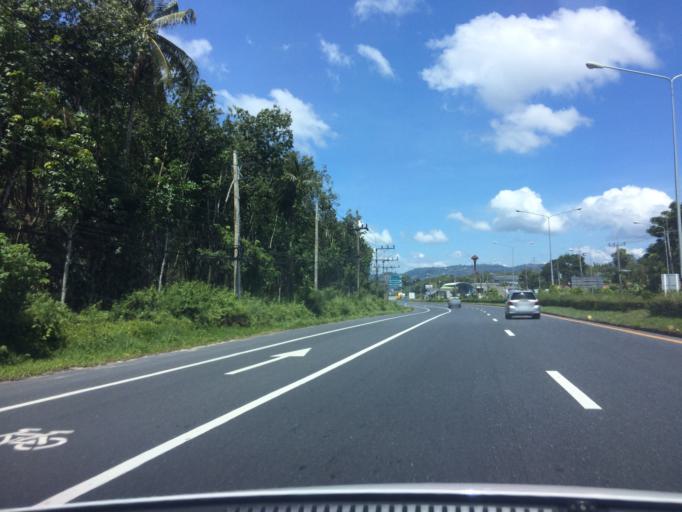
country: TH
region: Phangnga
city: Thai Mueang
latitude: 8.2378
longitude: 98.2970
